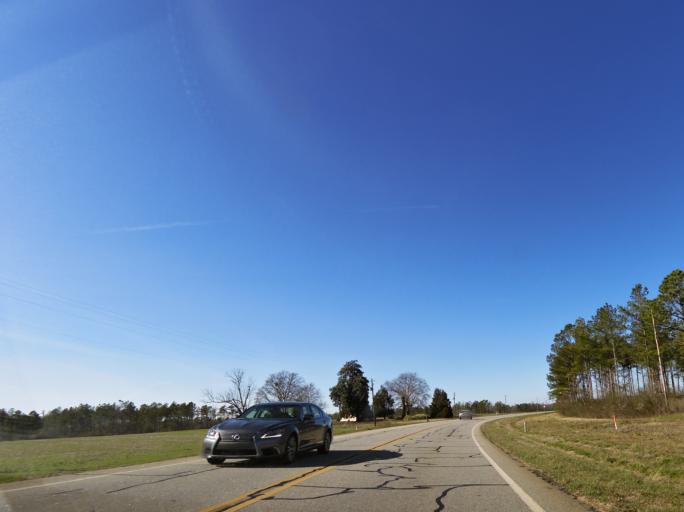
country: US
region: Georgia
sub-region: Lamar County
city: Barnesville
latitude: 32.8906
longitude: -84.1053
